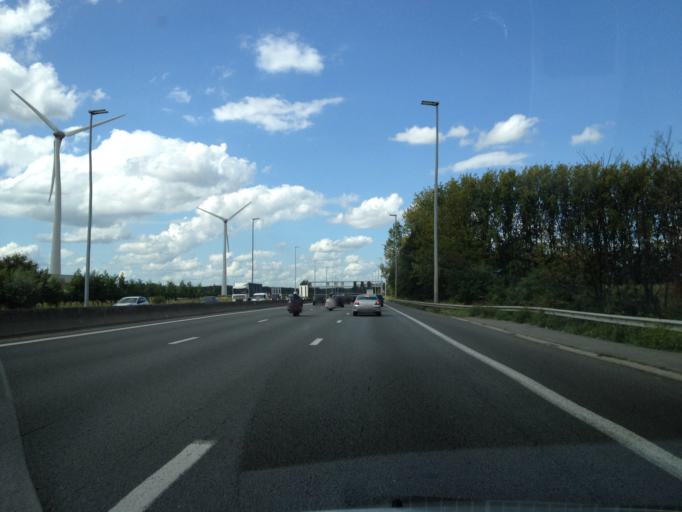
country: BE
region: Flanders
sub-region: Provincie Oost-Vlaanderen
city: Melle
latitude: 50.9803
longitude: 3.8228
